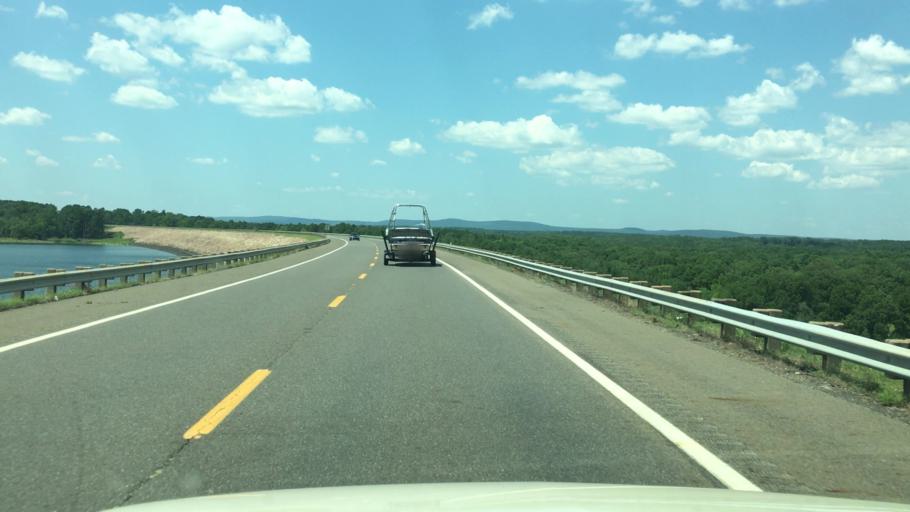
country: US
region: Arkansas
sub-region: Clark County
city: Arkadelphia
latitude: 34.2393
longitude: -93.1033
